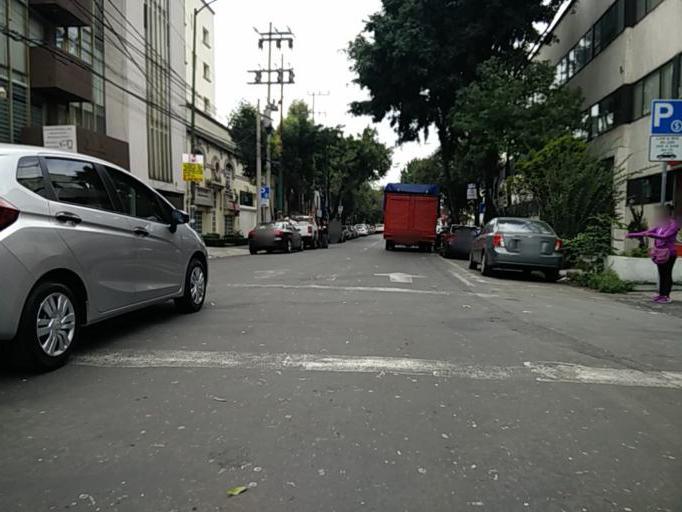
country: MX
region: Mexico City
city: Benito Juarez
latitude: 19.4207
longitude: -99.1713
